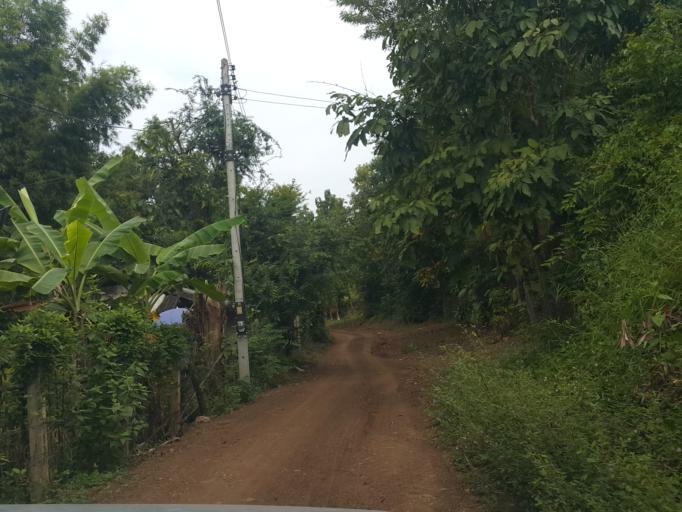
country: TH
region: Chiang Mai
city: Pai
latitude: 19.3630
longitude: 98.4508
